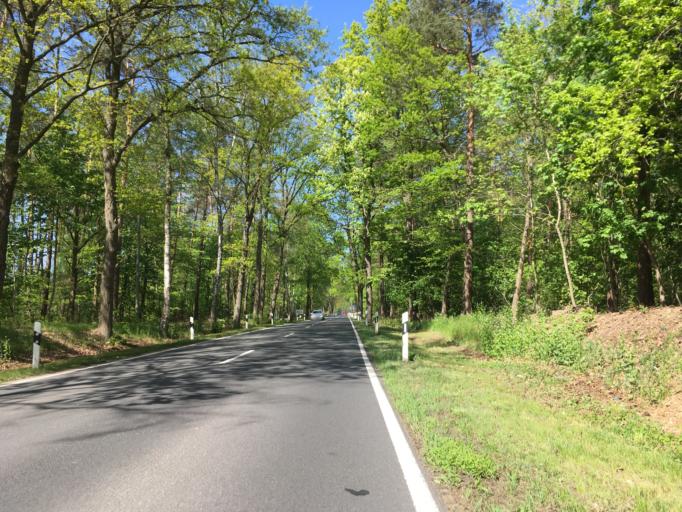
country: DE
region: Brandenburg
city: Rudnitz
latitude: 52.7673
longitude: 13.5652
